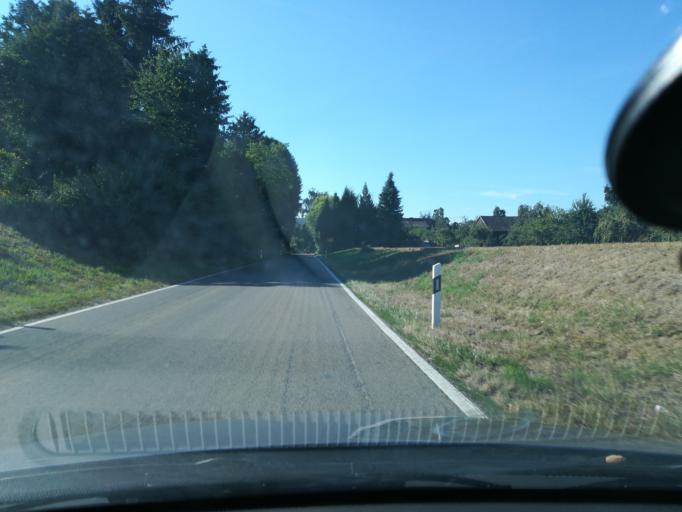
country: DE
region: Baden-Wuerttemberg
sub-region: Freiburg Region
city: Moos
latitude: 47.7140
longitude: 8.8957
